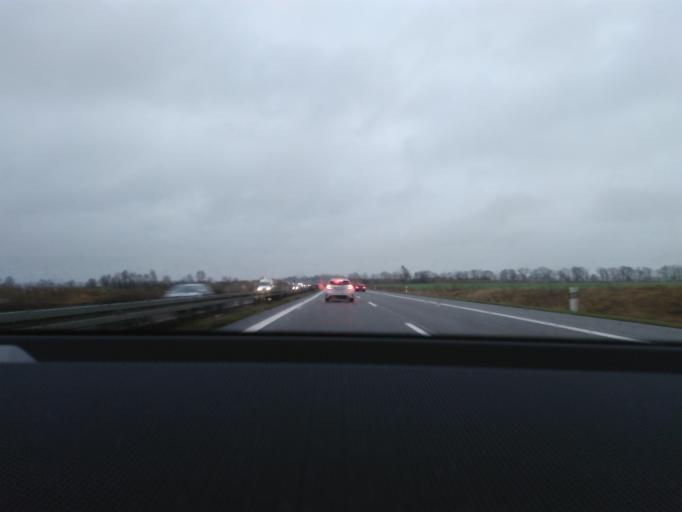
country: DE
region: Brandenburg
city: Heiligengrabe
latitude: 53.1828
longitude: 12.2952
